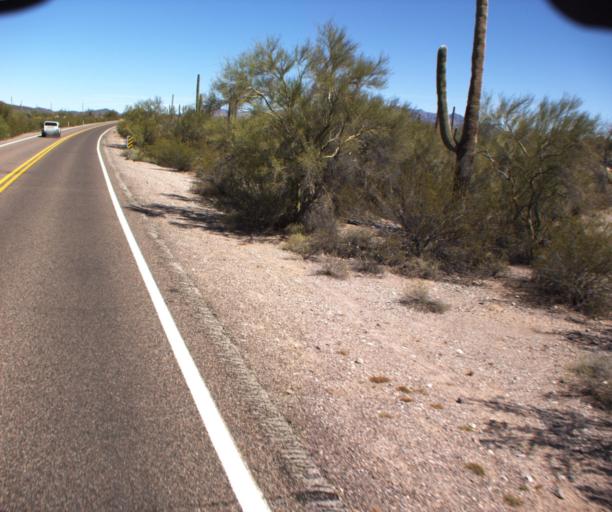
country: MX
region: Sonora
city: Sonoyta
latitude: 31.9079
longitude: -112.8106
